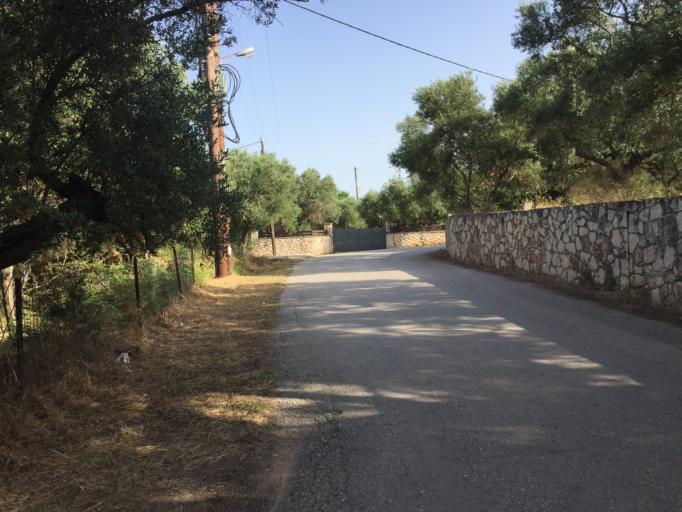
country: GR
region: Ionian Islands
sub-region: Nomos Zakynthou
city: Vanaton
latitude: 37.8243
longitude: 20.8567
